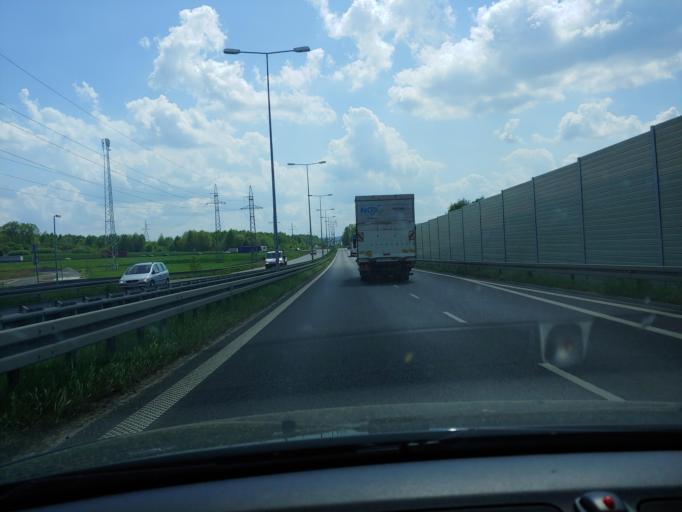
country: PL
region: Lesser Poland Voivodeship
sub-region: Powiat tarnowski
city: Lisia Gora
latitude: 50.0518
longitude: 21.0107
